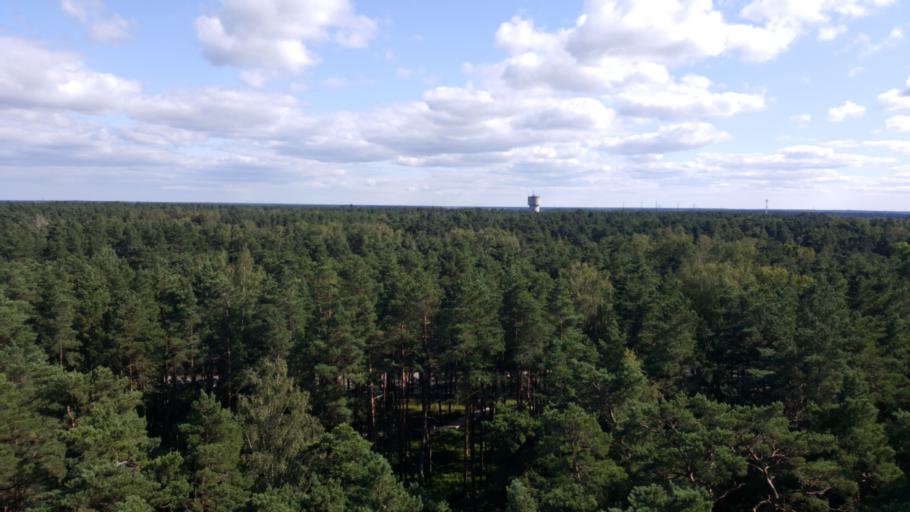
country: LV
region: Jurmala
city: Jurmala
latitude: 56.9764
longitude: 23.8212
